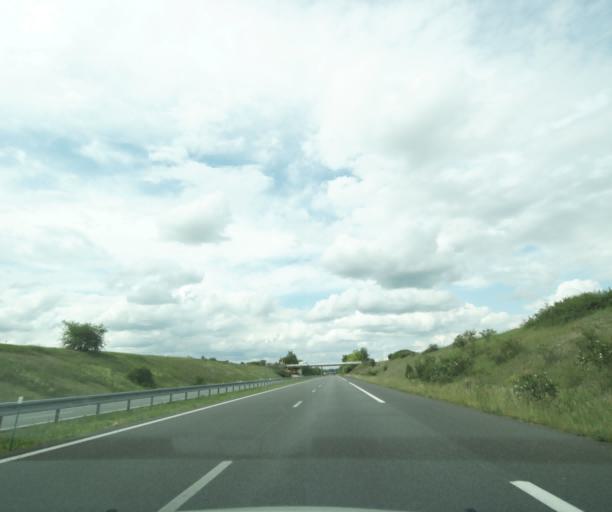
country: FR
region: Centre
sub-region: Departement du Cher
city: Mehun-sur-Yevre
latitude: 47.1527
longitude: 2.1843
